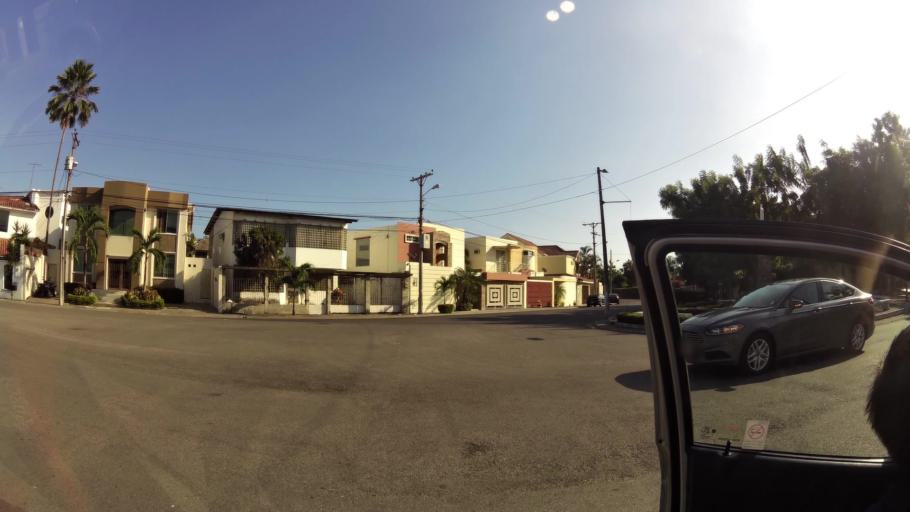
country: EC
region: Guayas
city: Santa Lucia
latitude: -2.1930
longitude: -79.9665
